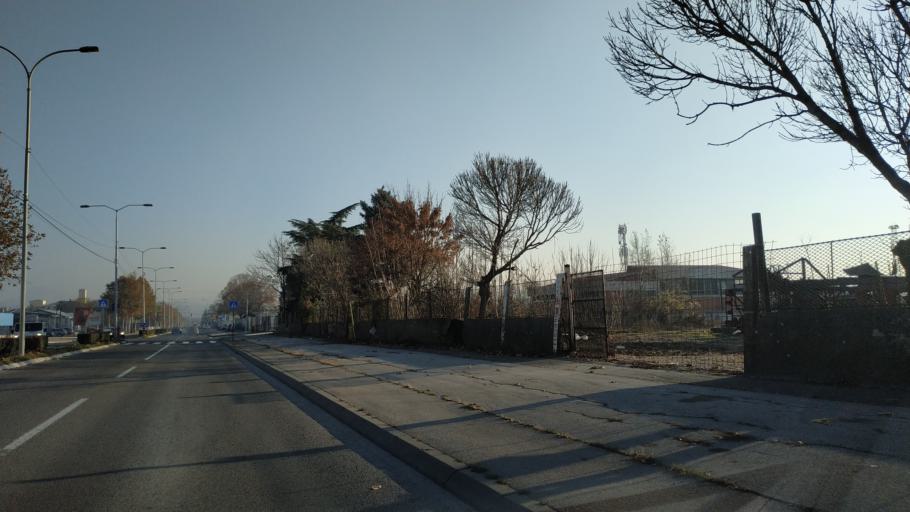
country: RS
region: Central Serbia
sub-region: Nisavski Okrug
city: Nis
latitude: 43.3368
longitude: 21.8776
